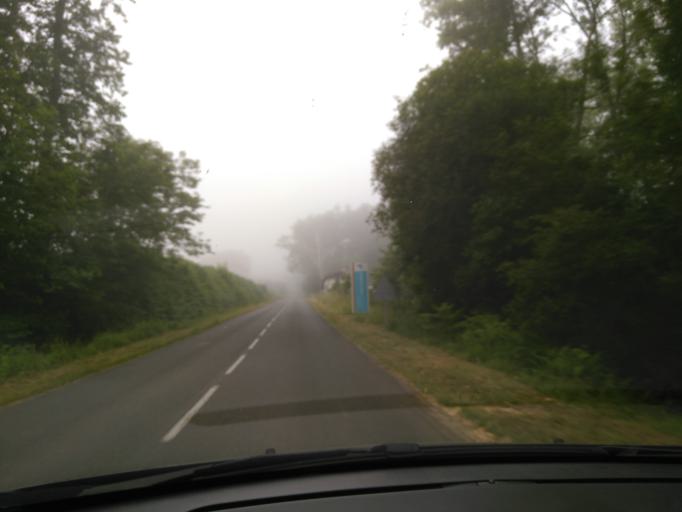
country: FR
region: Midi-Pyrenees
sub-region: Departement du Gers
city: Le Houga
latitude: 43.8604
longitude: -0.2047
